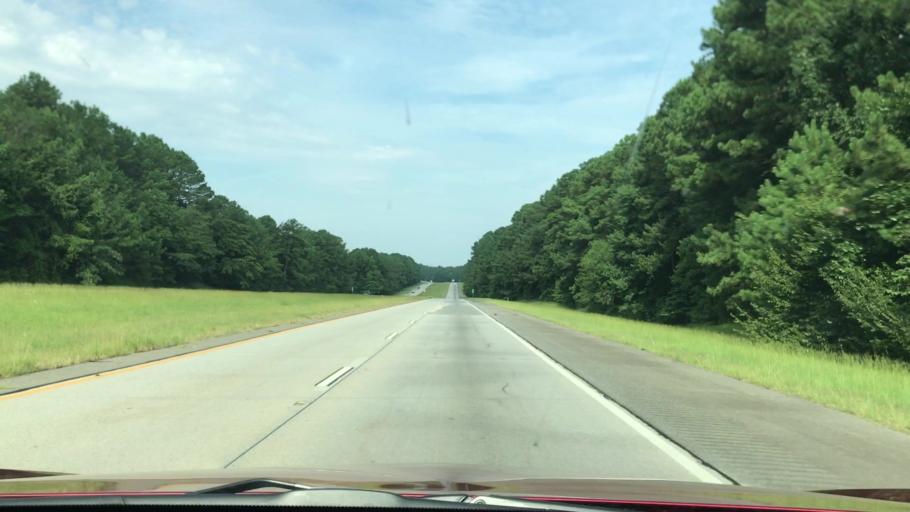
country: US
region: Georgia
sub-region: Warren County
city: Firing Range
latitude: 33.5043
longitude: -82.7549
